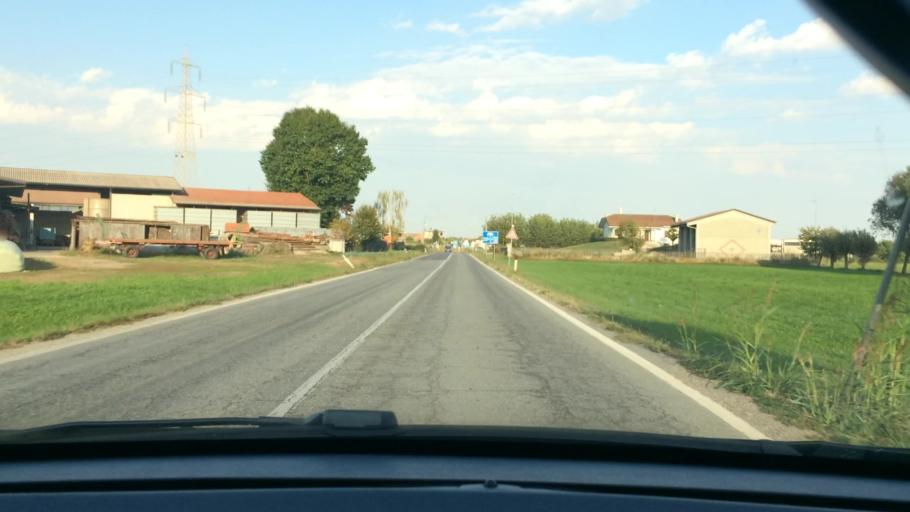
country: IT
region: Piedmont
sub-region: Provincia di Torino
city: Candiolo
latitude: 44.9532
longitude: 7.5809
